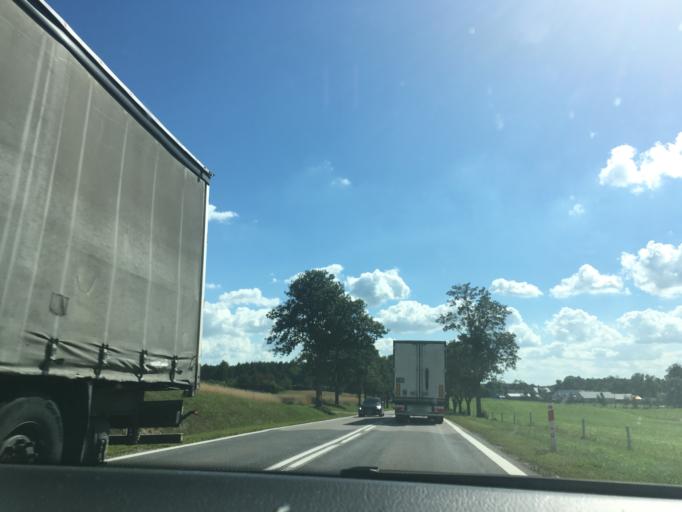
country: PL
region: Podlasie
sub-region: Powiat sokolski
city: Suchowola
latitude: 53.6171
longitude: 23.1234
